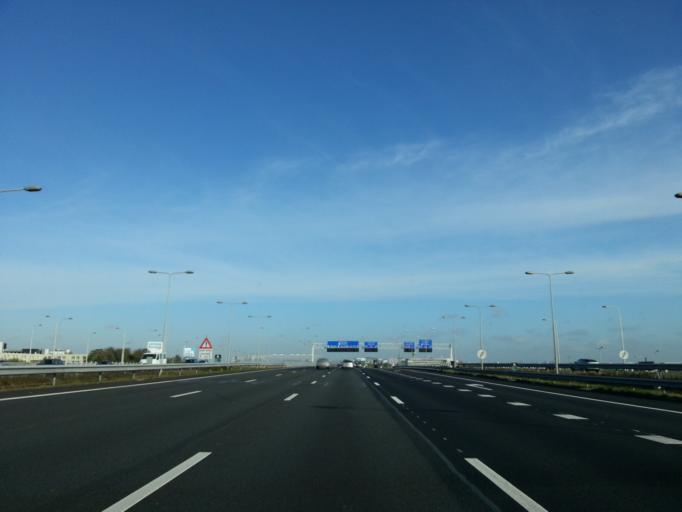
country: NL
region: North Holland
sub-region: Gemeente Haarlemmermeer
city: Hoofddorp
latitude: 52.2866
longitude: 4.7249
